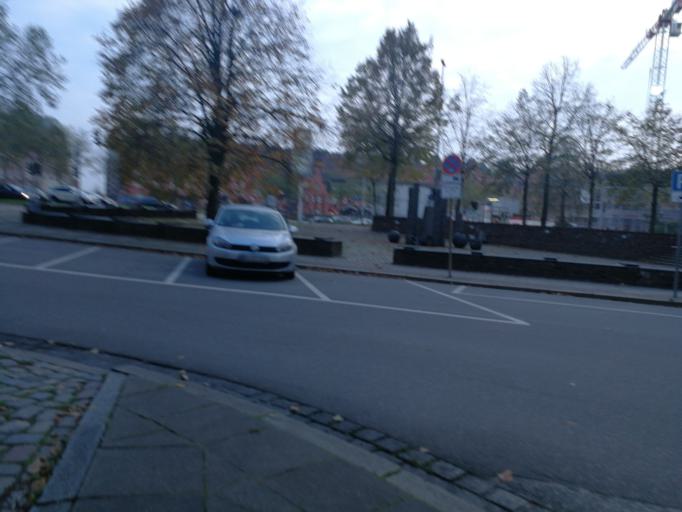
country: DE
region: Hamburg
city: Altstadt
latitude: 53.5482
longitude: 10.0006
